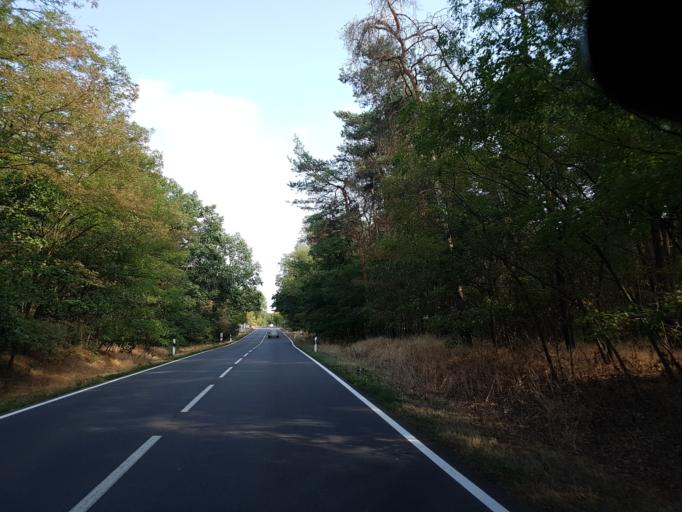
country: DE
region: Saxony-Anhalt
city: Pretzsch
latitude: 51.7325
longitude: 12.7711
